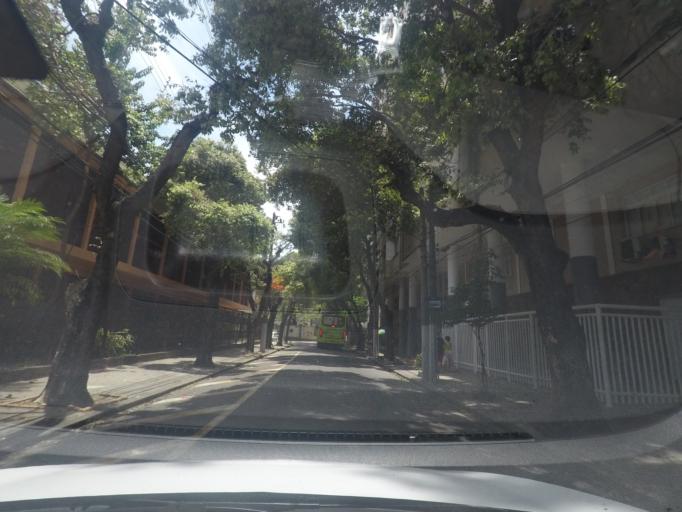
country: BR
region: Rio de Janeiro
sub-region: Niteroi
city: Niteroi
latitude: -22.9028
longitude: -43.1256
